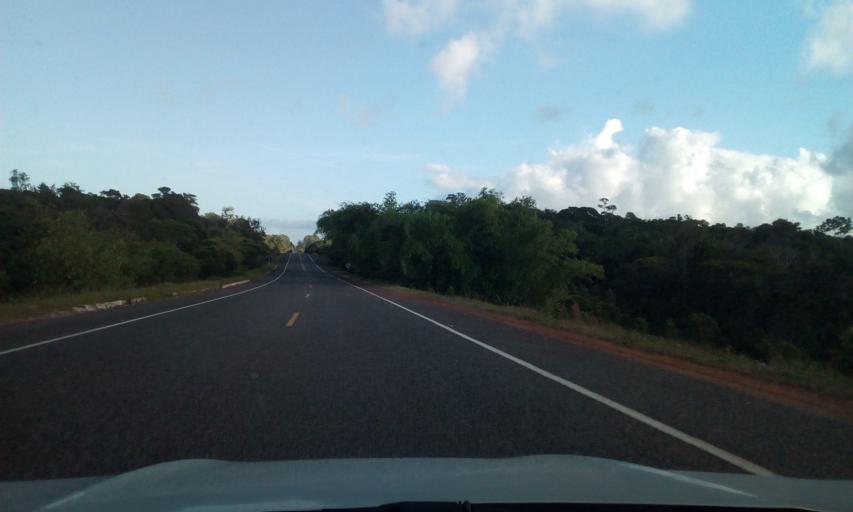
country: BR
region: Bahia
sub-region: Entre Rios
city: Entre Rios
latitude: -12.3356
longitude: -37.9043
